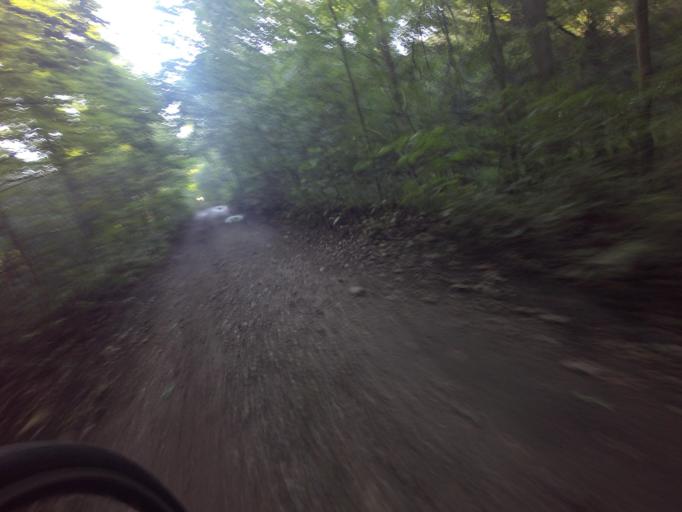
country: CA
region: Ontario
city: Goderich
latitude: 43.7536
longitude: -81.5694
